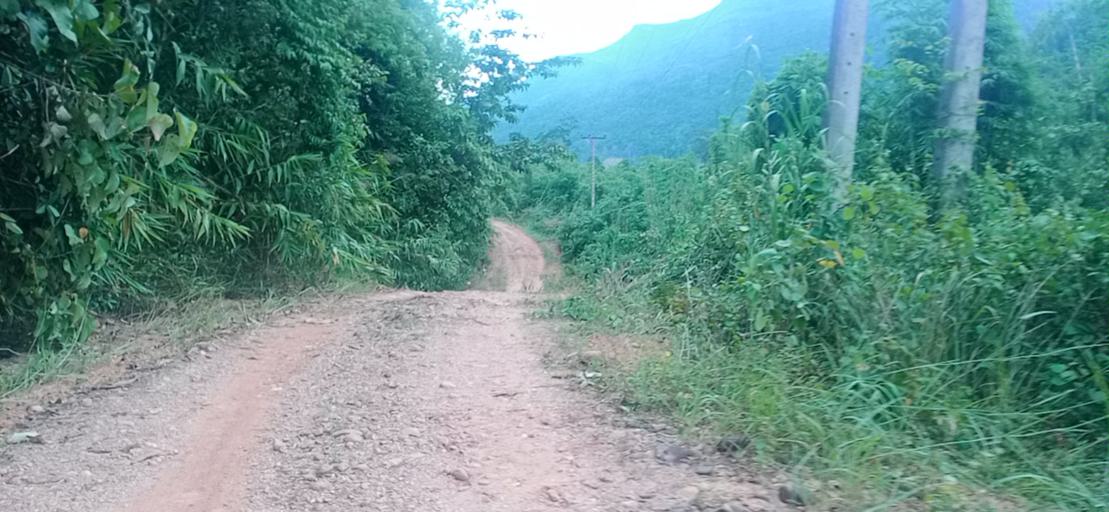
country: TH
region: Changwat Bueng Kan
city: Pak Khat
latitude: 18.5605
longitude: 103.2256
